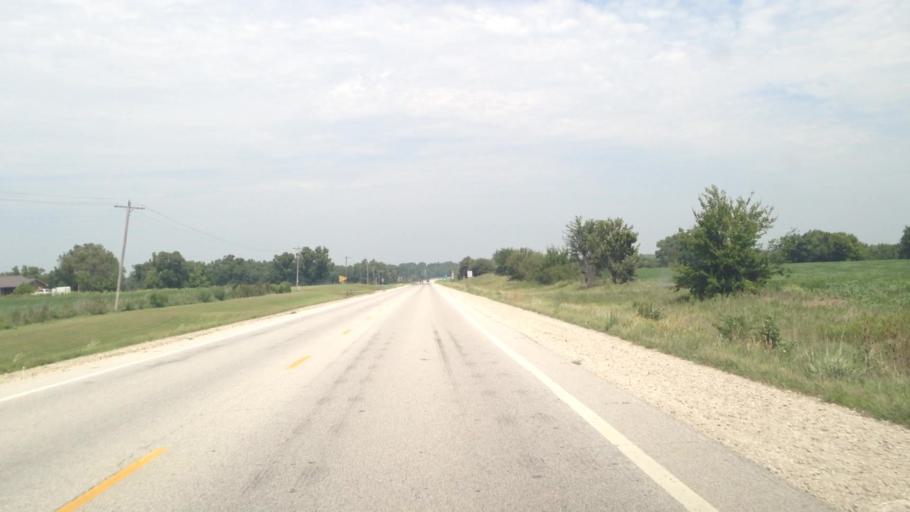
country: US
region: Kansas
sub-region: Neosho County
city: Erie
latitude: 37.5246
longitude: -95.2702
